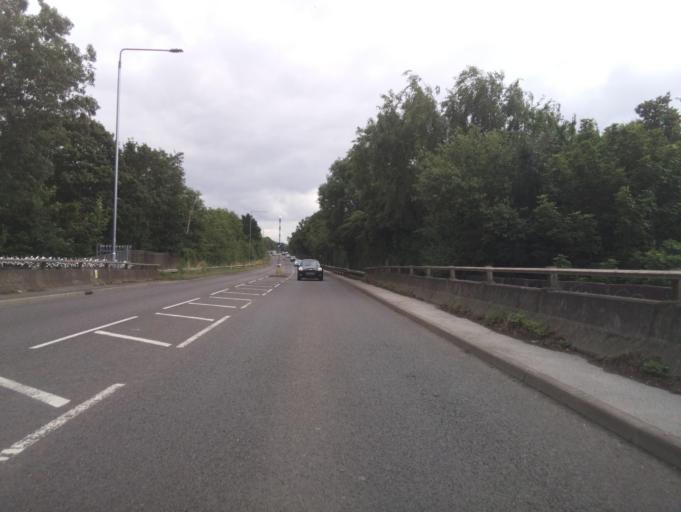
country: GB
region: England
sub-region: Nottinghamshire
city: Radcliffe on Trent
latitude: 52.9677
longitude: -1.0715
